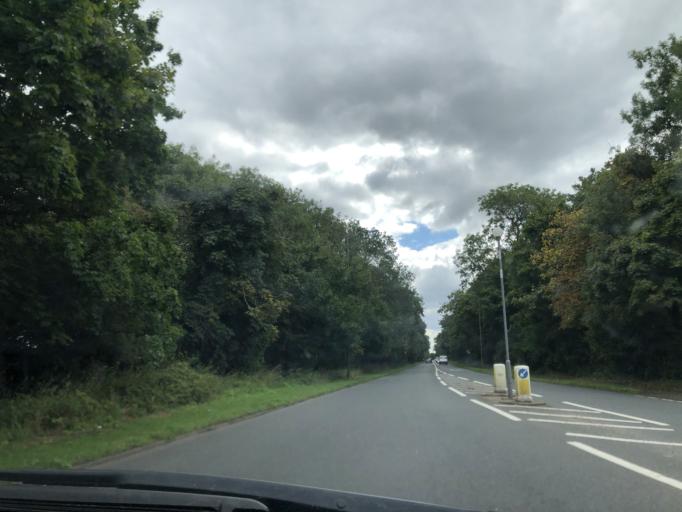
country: GB
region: England
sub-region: Kent
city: Halstead
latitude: 51.3563
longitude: 0.1256
